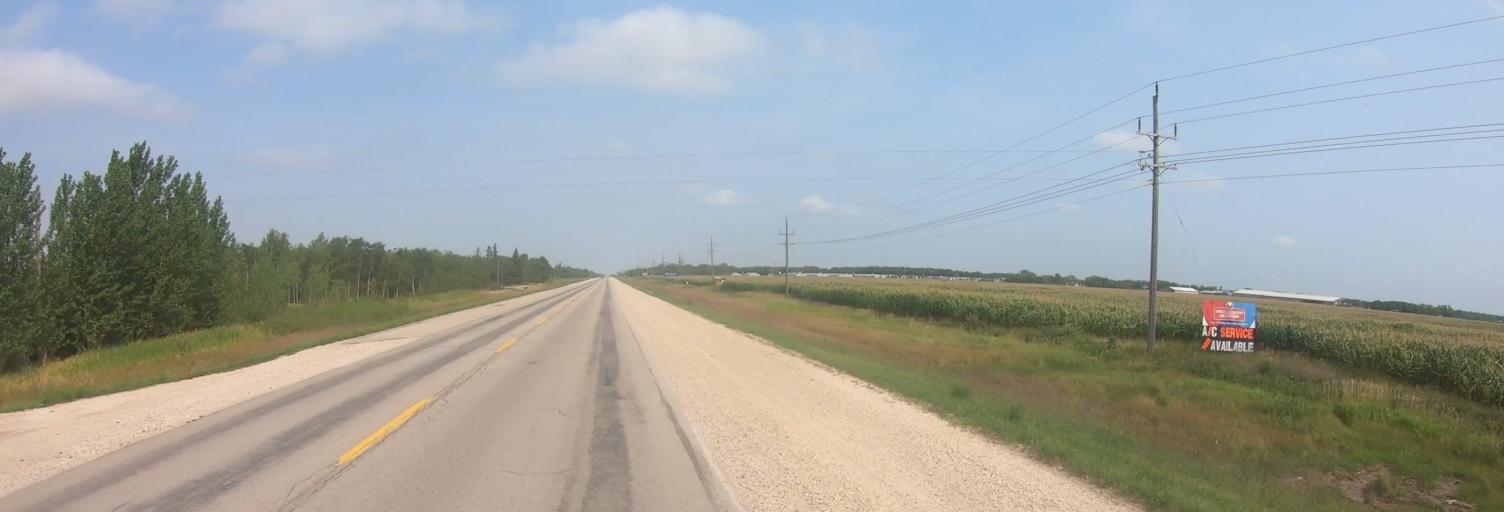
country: CA
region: Manitoba
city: Steinbach
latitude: 49.4813
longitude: -96.6911
